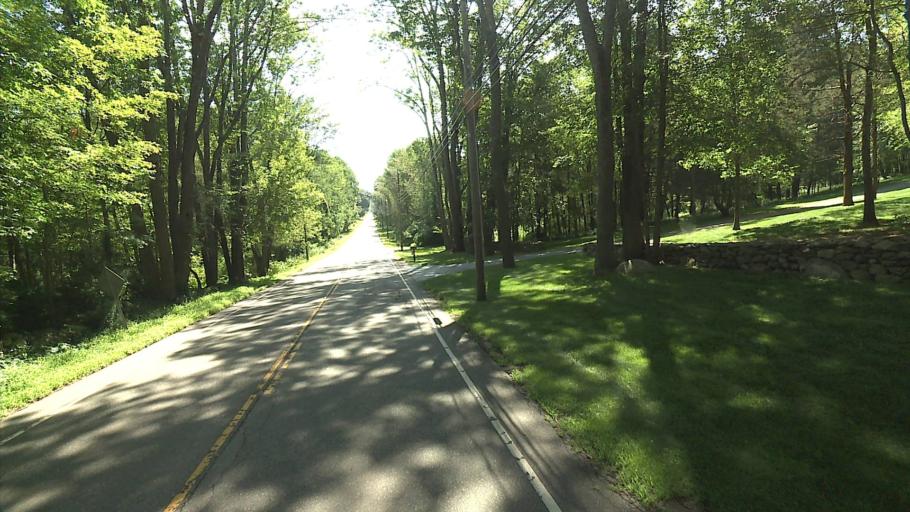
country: US
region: Connecticut
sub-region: Windham County
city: Windham
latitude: 41.6974
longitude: -72.1303
